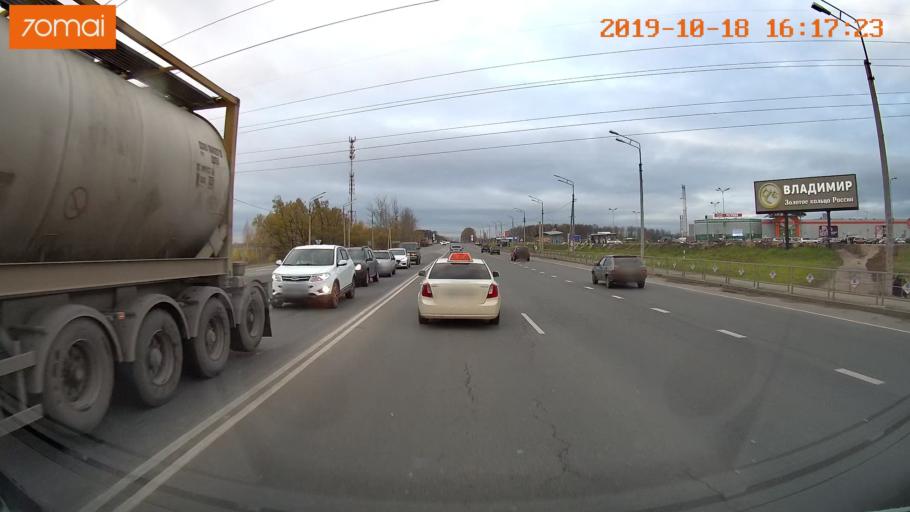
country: RU
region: Vladimir
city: Kommunar
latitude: 56.1744
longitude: 40.4581
